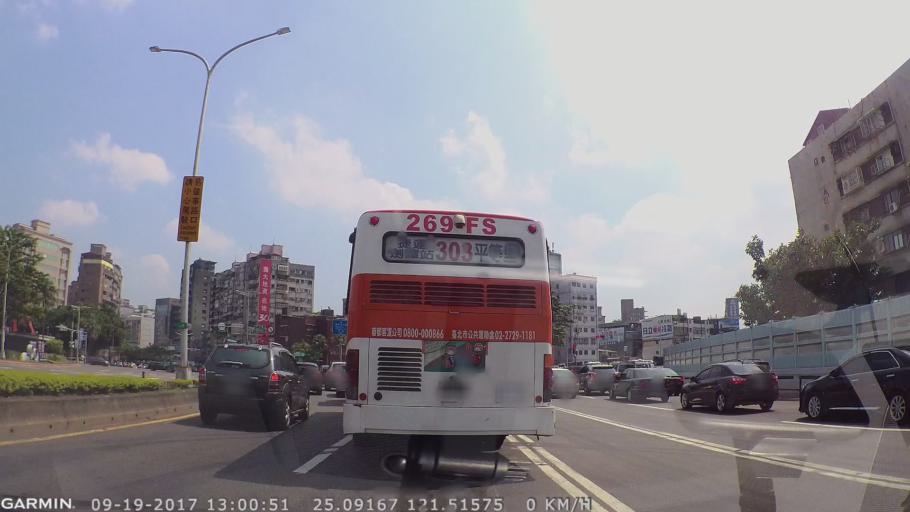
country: TW
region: Taipei
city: Taipei
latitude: 25.1020
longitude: 121.5140
